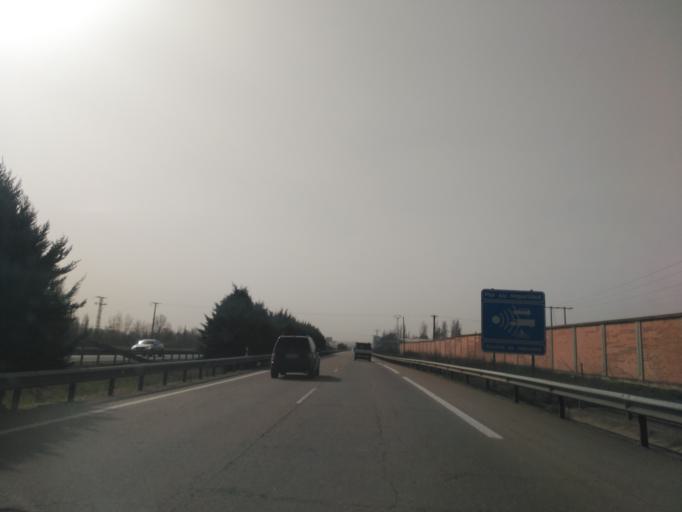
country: ES
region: Castille and Leon
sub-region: Provincia de Valladolid
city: Santovenia de Pisuerga
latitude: 41.7255
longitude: -4.6879
